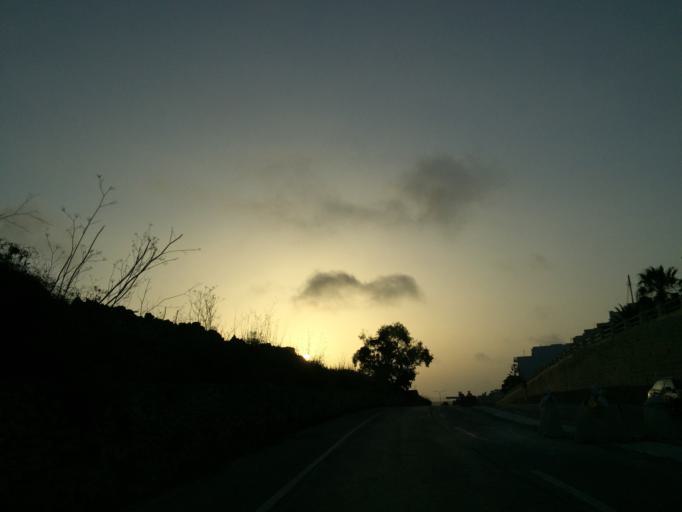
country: MT
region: Il-Mellieha
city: Mellieha
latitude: 35.9541
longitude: 14.3609
